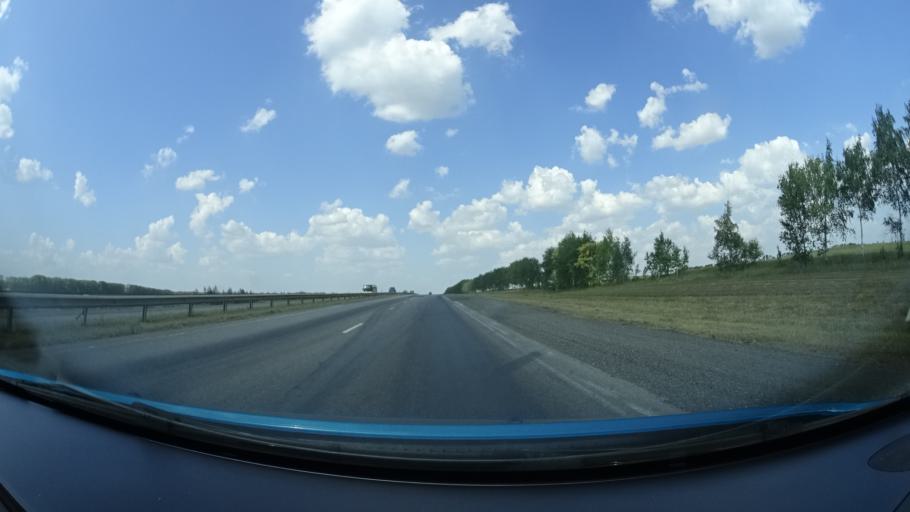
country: RU
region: Bashkortostan
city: Alekseyevka
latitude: 54.7299
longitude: 55.1426
